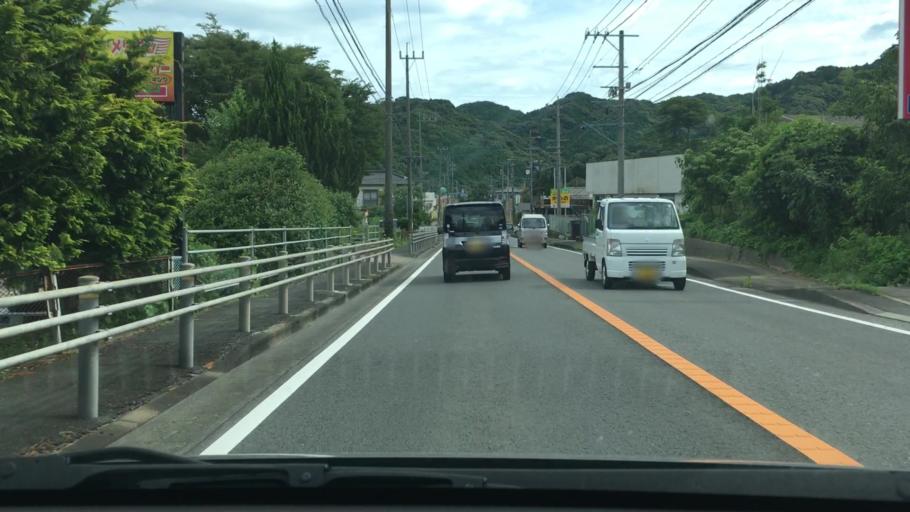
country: JP
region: Nagasaki
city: Togitsu
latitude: 32.8979
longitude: 129.7809
